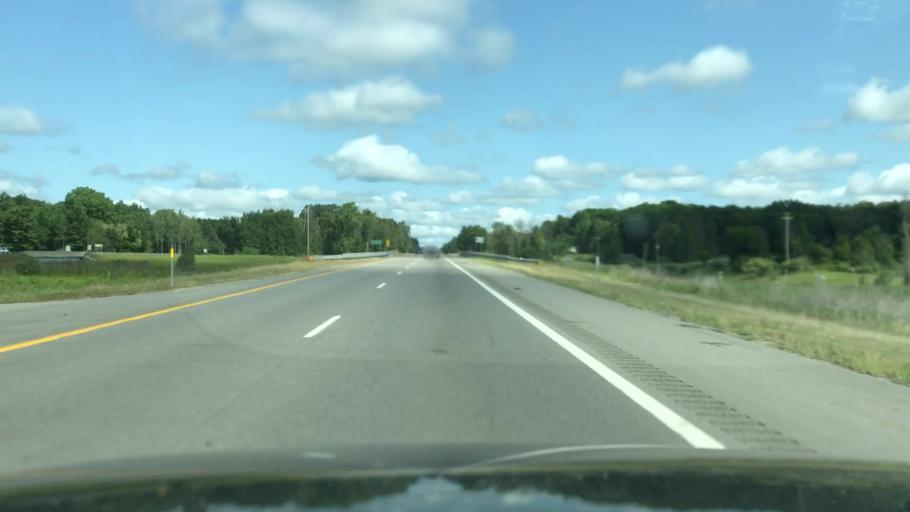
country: US
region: Michigan
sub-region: Mecosta County
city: Big Rapids
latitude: 43.6260
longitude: -85.5006
